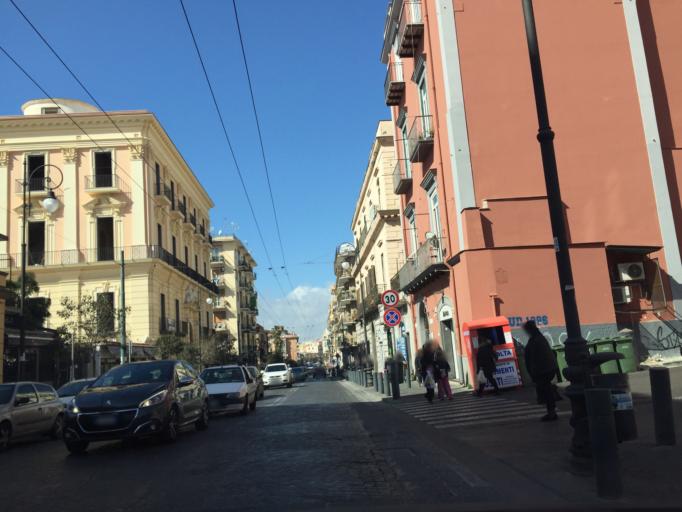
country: IT
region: Campania
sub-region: Provincia di Napoli
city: Portici
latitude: 40.8165
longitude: 14.3335
